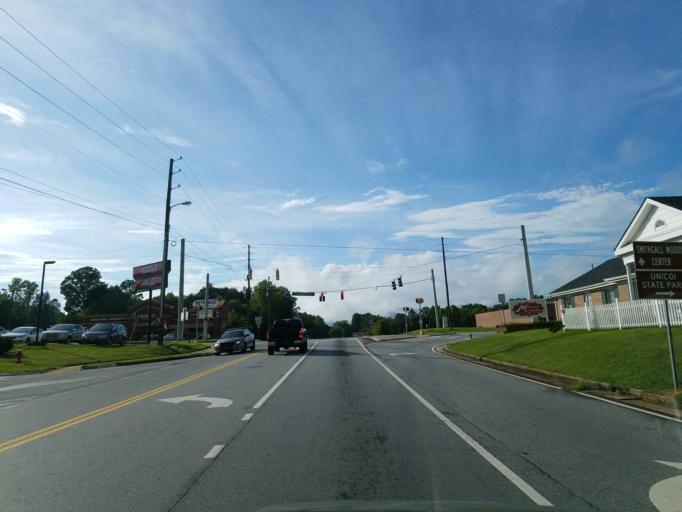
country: US
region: Georgia
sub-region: White County
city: Cleveland
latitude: 34.6013
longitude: -83.7649
